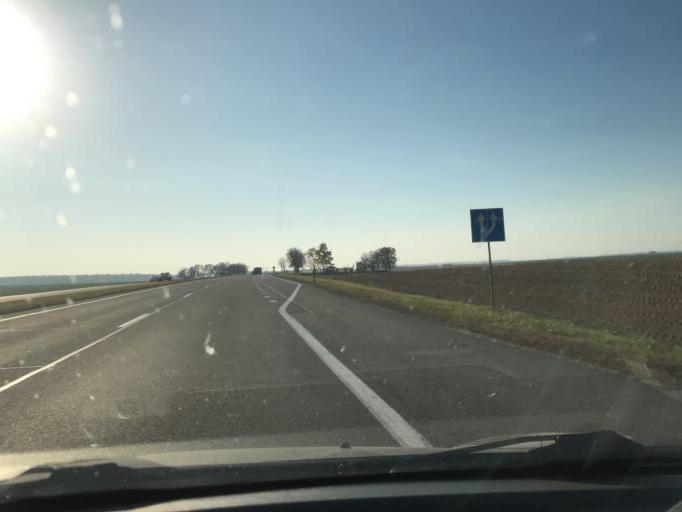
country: BY
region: Minsk
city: Hatava
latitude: 53.7434
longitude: 27.6267
